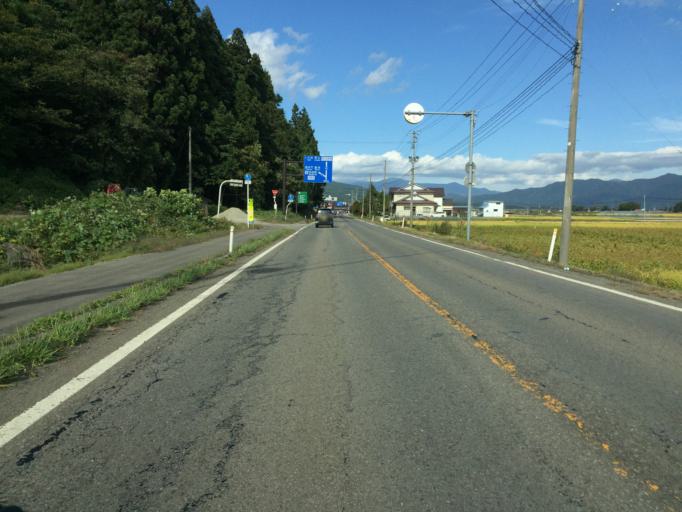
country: JP
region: Fukushima
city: Inawashiro
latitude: 37.5329
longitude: 140.0588
